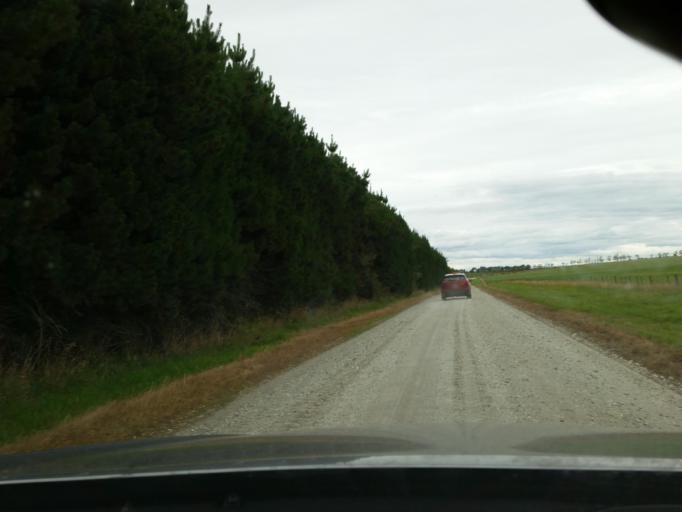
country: NZ
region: Southland
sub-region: Invercargill City
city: Invercargill
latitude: -46.3874
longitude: 168.5903
